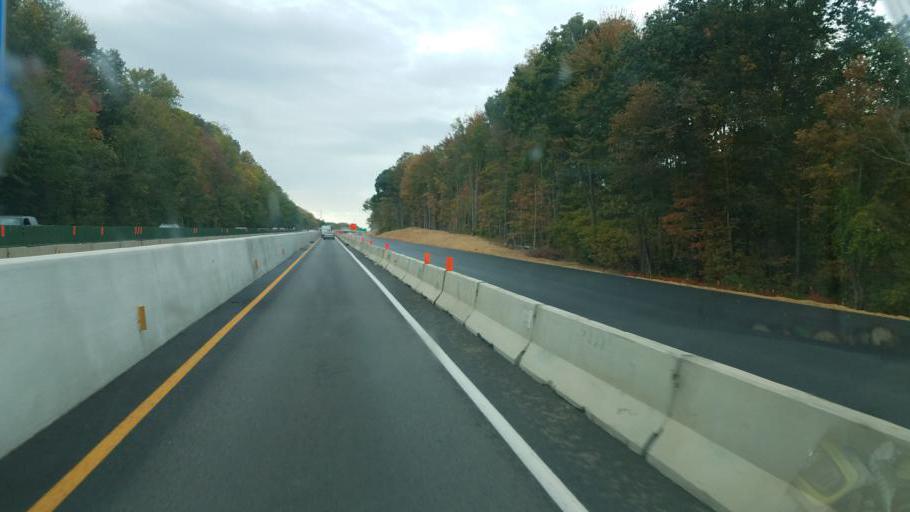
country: US
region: Ohio
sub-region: Summit County
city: Norton
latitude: 41.0395
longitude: -81.6259
